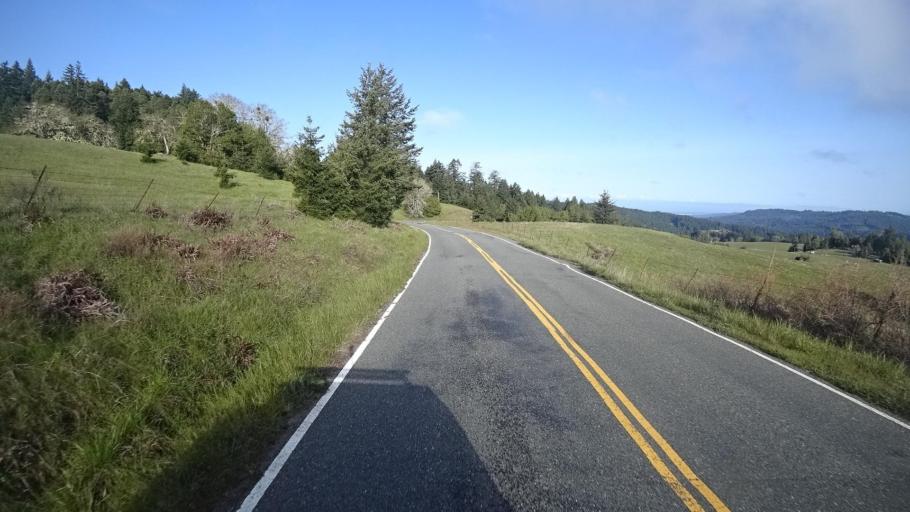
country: US
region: California
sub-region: Humboldt County
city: Blue Lake
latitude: 40.7378
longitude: -123.9479
